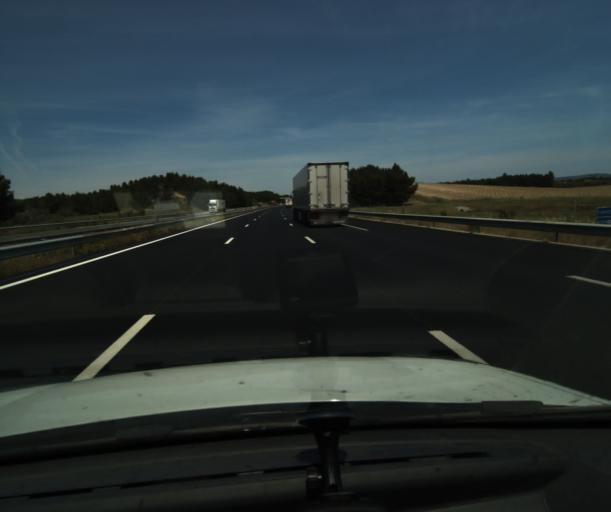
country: FR
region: Languedoc-Roussillon
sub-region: Departement de l'Aude
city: Peyriac-de-Mer
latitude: 43.1002
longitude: 2.9427
